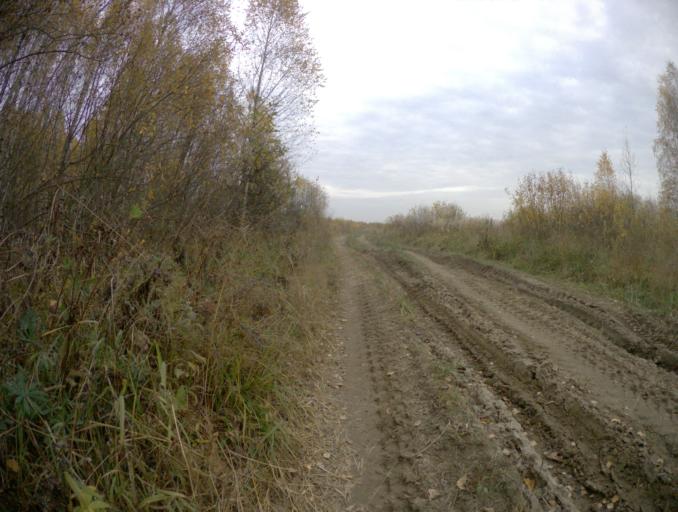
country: RU
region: Vladimir
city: Golovino
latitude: 55.9381
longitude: 40.3787
